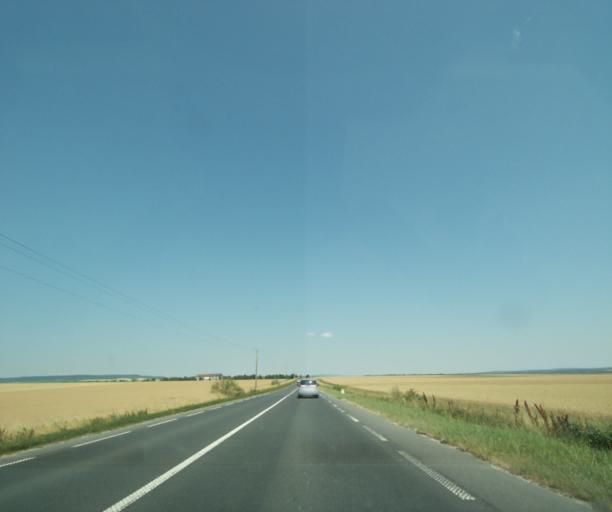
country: FR
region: Champagne-Ardenne
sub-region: Departement de la Marne
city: Mourmelon-le-Grand
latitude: 49.0793
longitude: 4.2837
